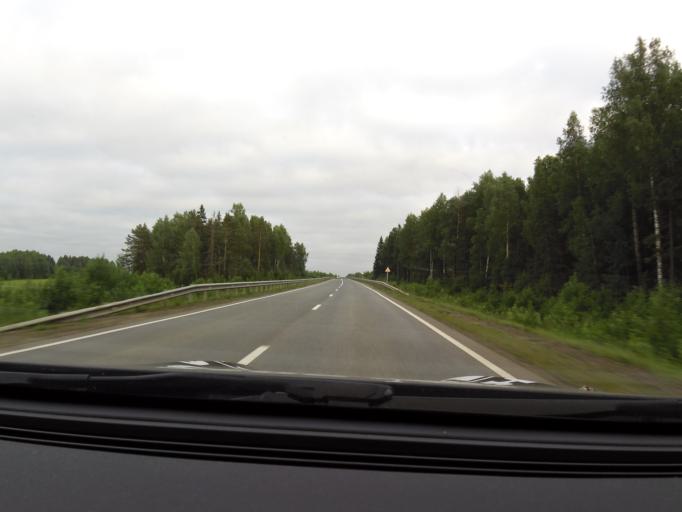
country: RU
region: Perm
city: Siva
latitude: 58.4314
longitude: 54.4421
